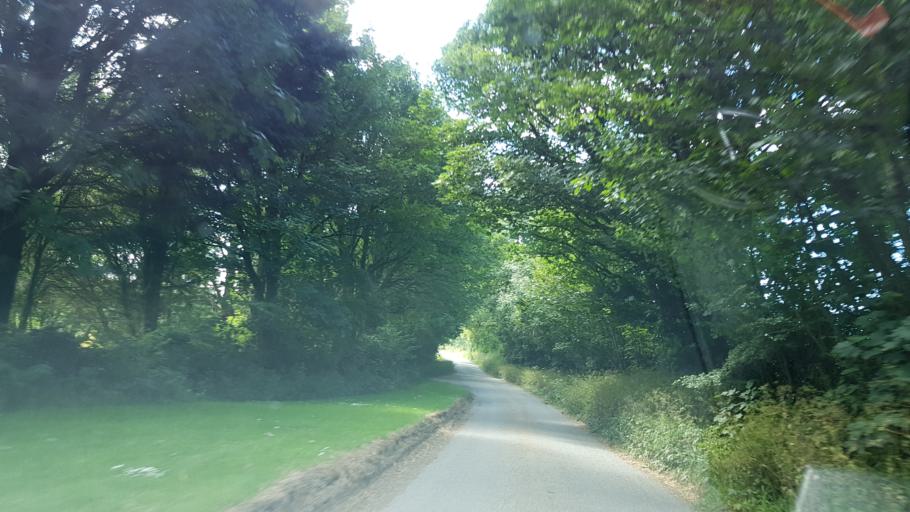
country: GB
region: Wales
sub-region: Pembrokeshire
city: Wiston
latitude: 51.8281
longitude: -4.8832
